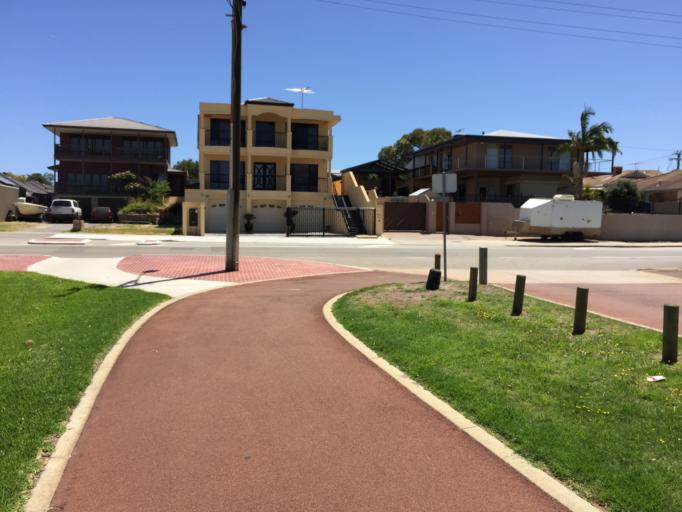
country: AU
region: Western Australia
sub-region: Canning
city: Wilson
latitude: -32.0286
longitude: 115.9004
